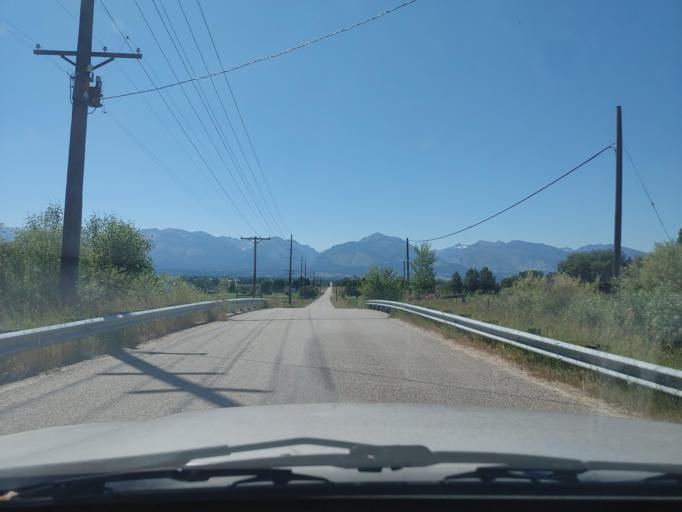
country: US
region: Montana
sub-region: Ravalli County
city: Hamilton
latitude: 46.2768
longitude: -114.0544
